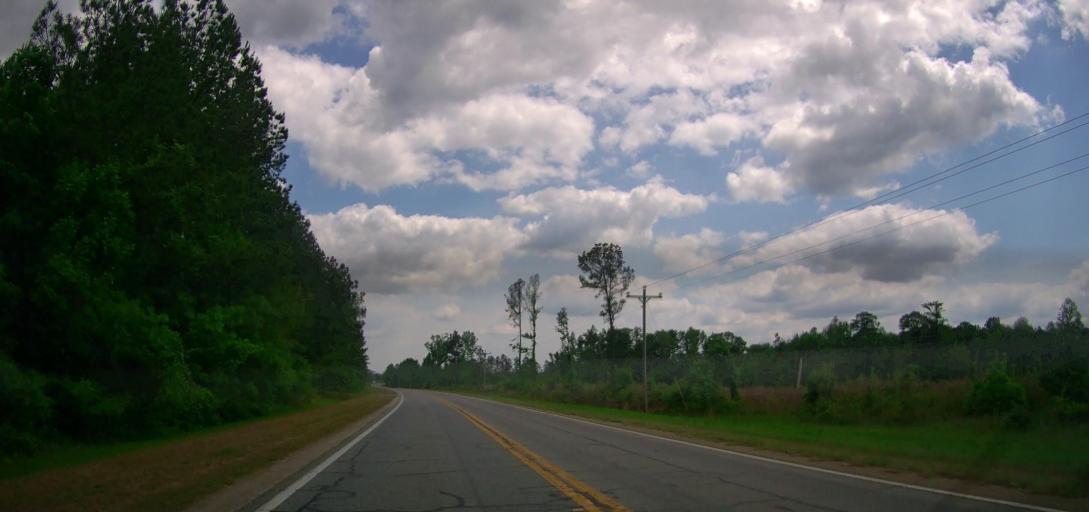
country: US
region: Georgia
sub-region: Laurens County
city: East Dublin
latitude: 32.4910
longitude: -82.8268
